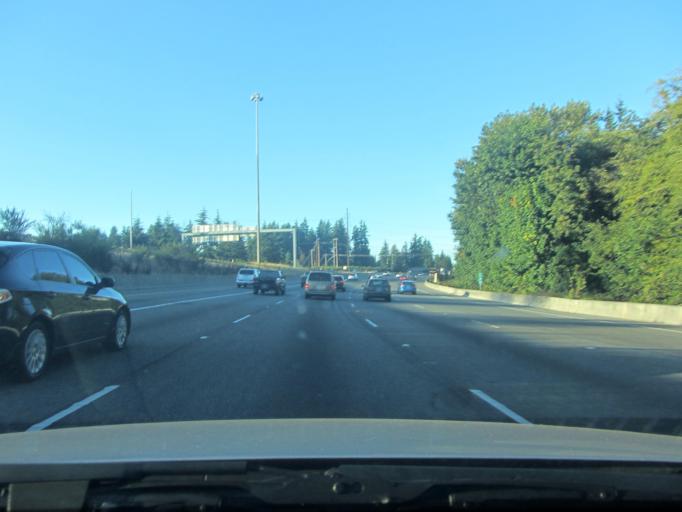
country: US
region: Washington
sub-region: Snohomish County
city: Everett
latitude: 47.9259
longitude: -122.2031
